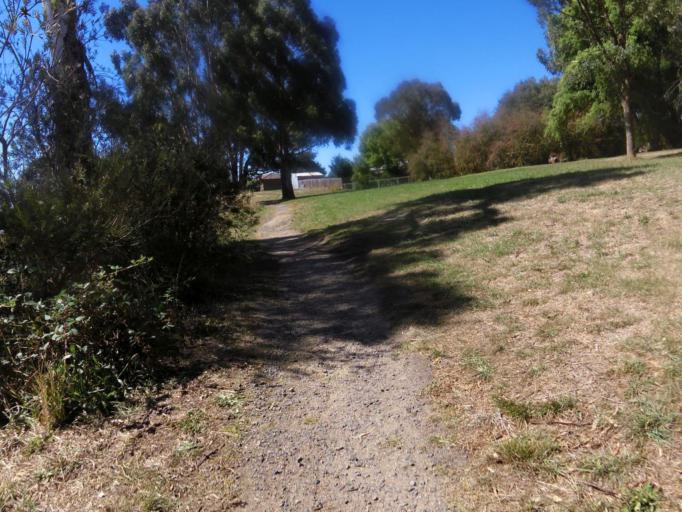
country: AU
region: Victoria
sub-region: Mount Alexander
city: Castlemaine
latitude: -37.2480
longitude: 144.4419
